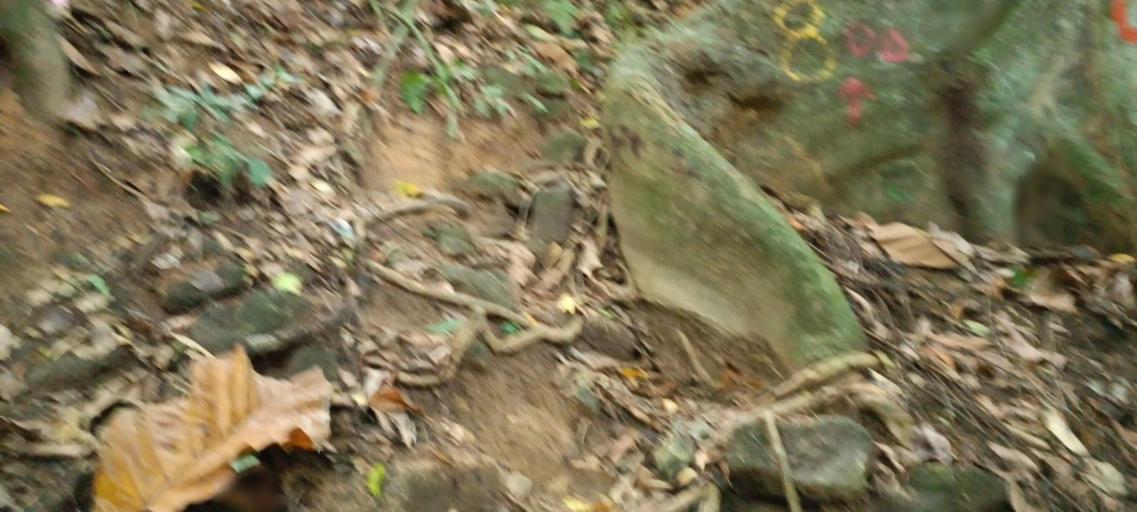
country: MY
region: Penang
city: Bukit Mertajam
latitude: 5.3659
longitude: 100.4949
